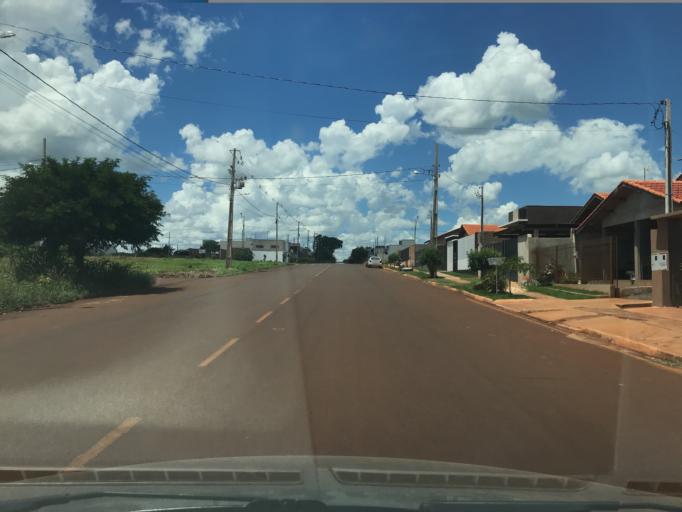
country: BR
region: Parana
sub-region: Palotina
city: Palotina
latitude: -24.2648
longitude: -53.8461
